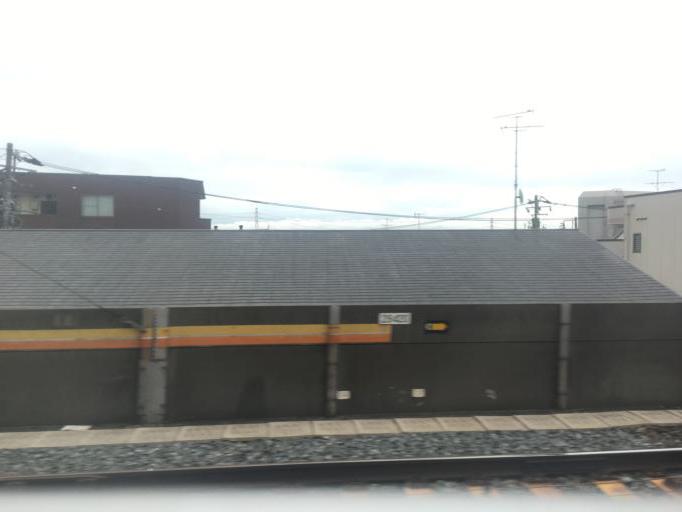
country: JP
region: Chiba
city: Funabashi
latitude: 35.7047
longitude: 139.9434
